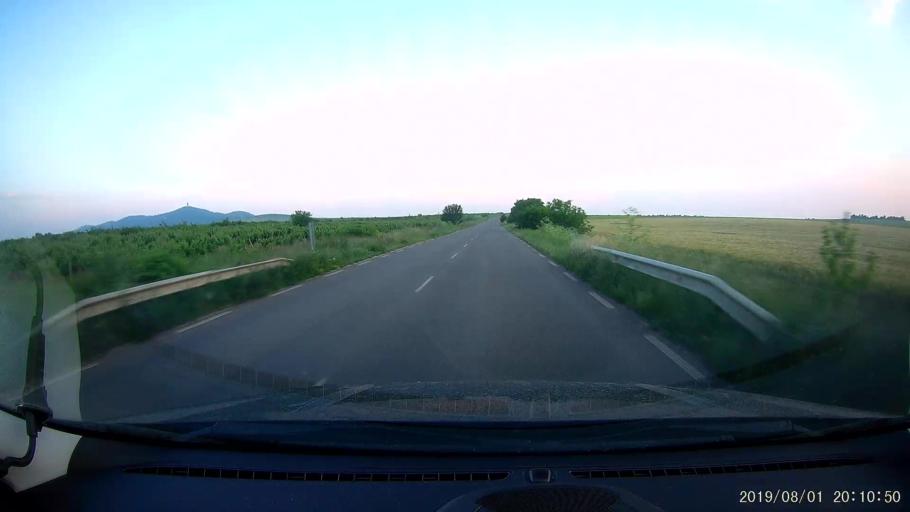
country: BG
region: Yambol
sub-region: Obshtina Yambol
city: Yambol
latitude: 42.4736
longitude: 26.6031
